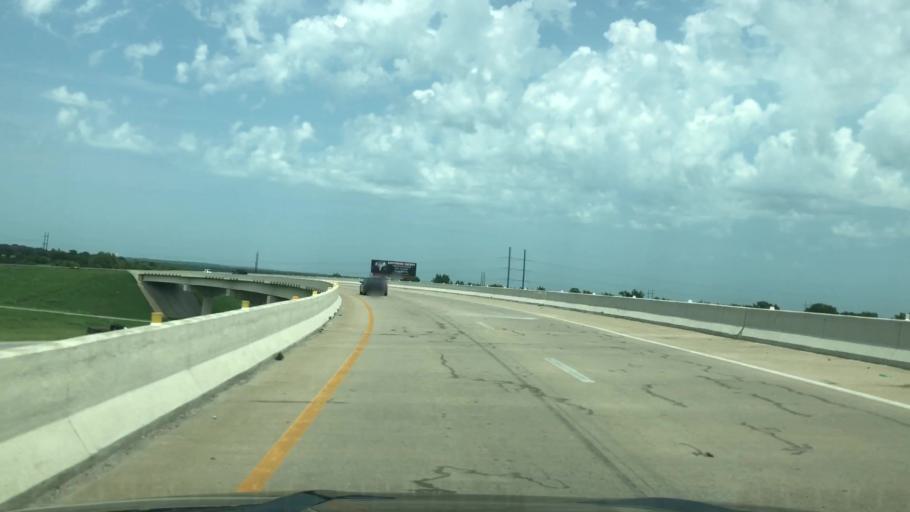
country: US
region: Oklahoma
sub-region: Rogers County
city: Catoosa
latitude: 36.1632
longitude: -95.7320
